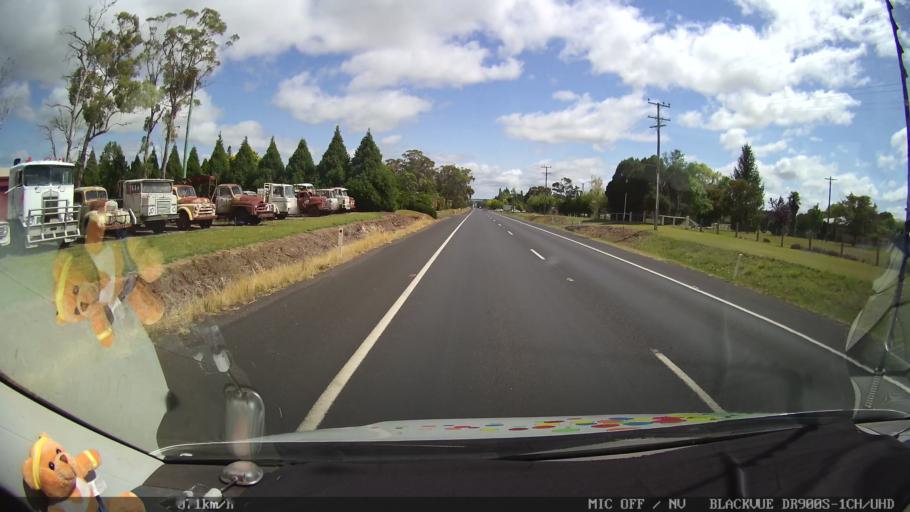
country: AU
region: New South Wales
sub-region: Glen Innes Severn
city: Glen Innes
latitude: -29.7638
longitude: 151.7334
